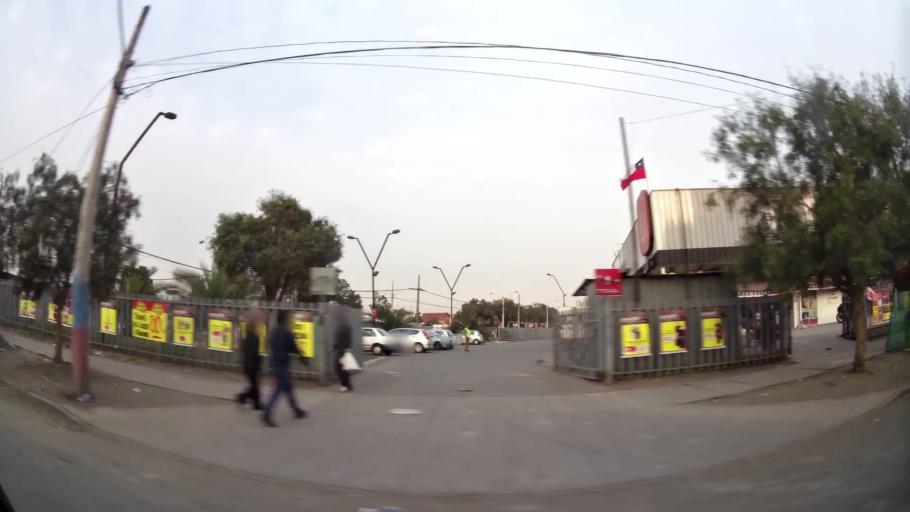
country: CL
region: Santiago Metropolitan
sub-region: Provincia de Santiago
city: Lo Prado
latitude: -33.5074
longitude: -70.7841
